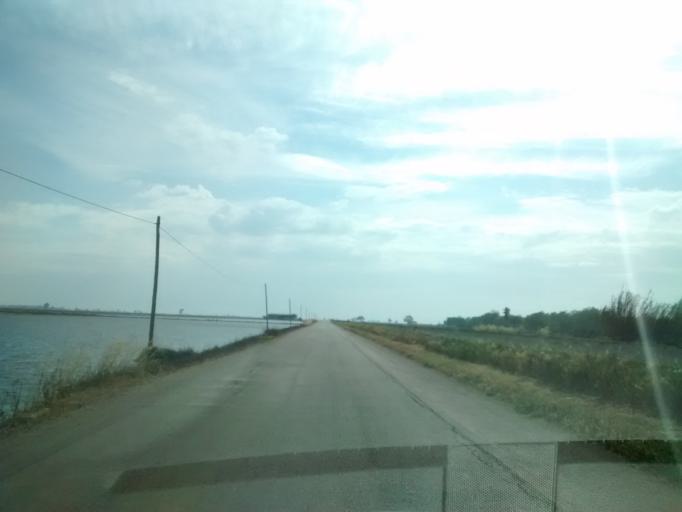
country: ES
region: Catalonia
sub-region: Provincia de Tarragona
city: Deltebre
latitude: 40.6982
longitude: 0.8091
